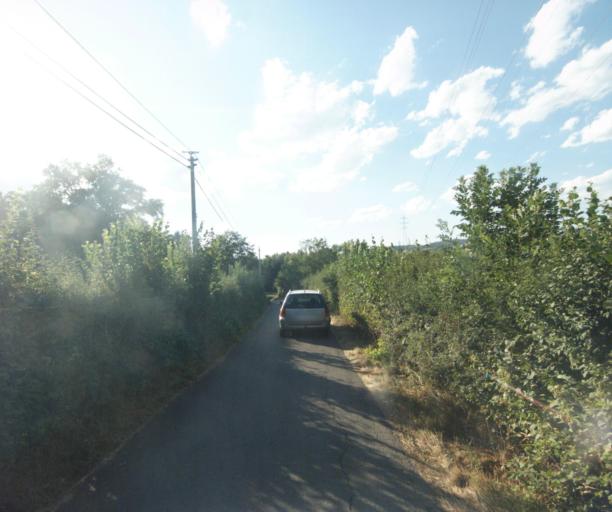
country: FR
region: Rhone-Alpes
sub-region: Departement du Rhone
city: Lozanne
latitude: 45.8472
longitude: 4.6877
